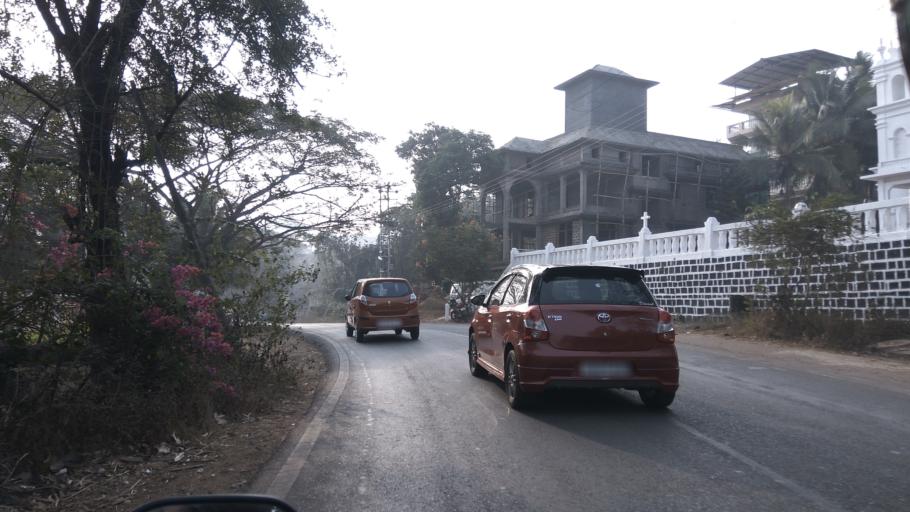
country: IN
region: Goa
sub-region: North Goa
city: Saligao
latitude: 15.5448
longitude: 73.8060
